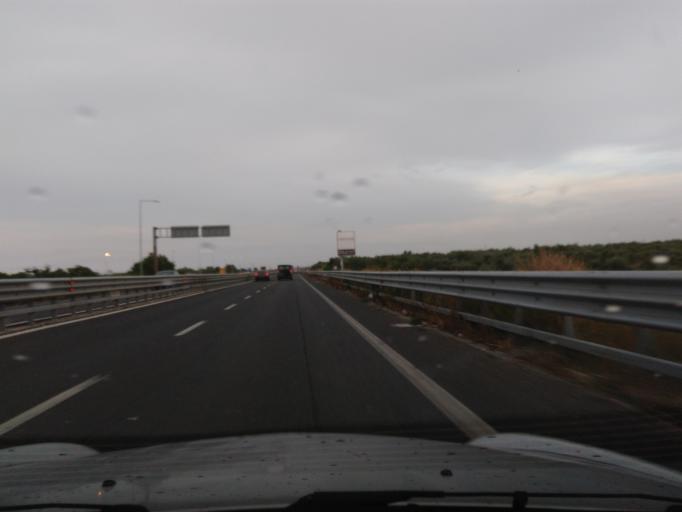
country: IT
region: Apulia
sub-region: Provincia di Bari
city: Giovinazzo
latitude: 41.1738
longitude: 16.6764
